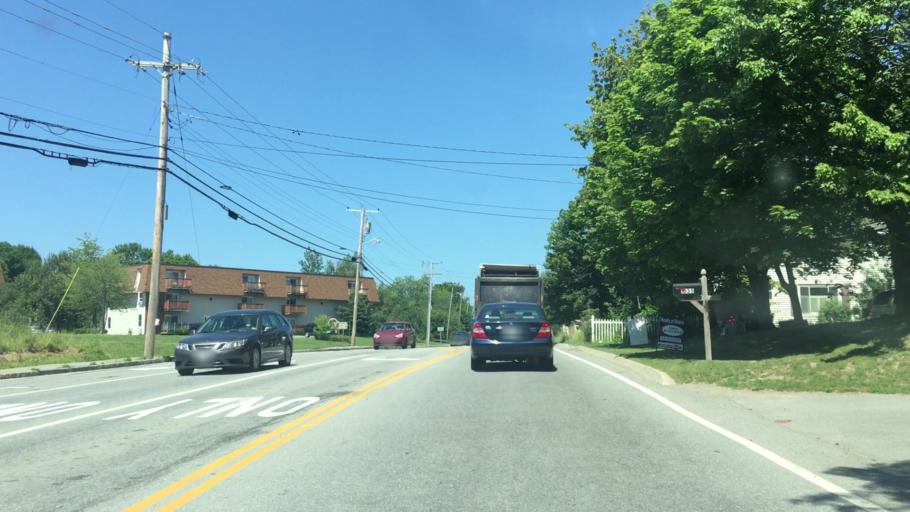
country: US
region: Maine
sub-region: Penobscot County
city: Bangor
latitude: 44.8247
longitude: -68.8093
